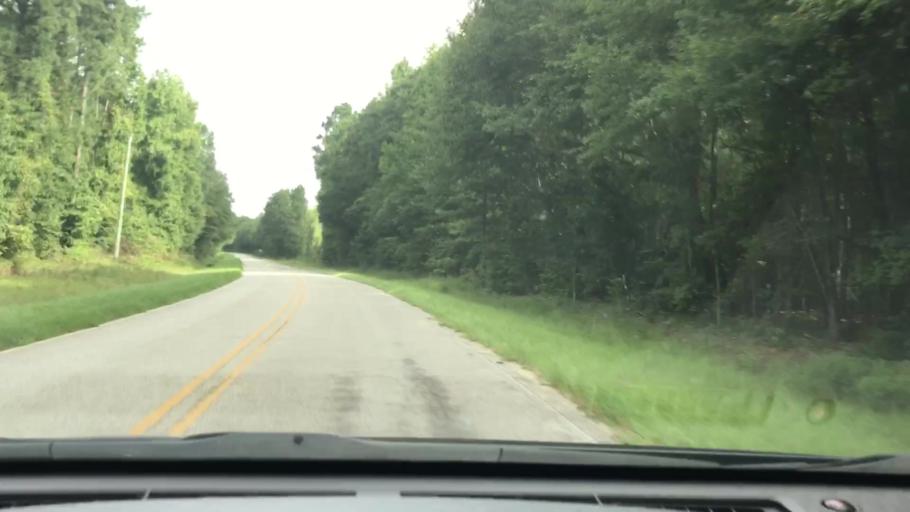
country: US
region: Georgia
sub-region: Jefferson County
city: Wadley
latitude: 32.8204
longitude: -82.3773
